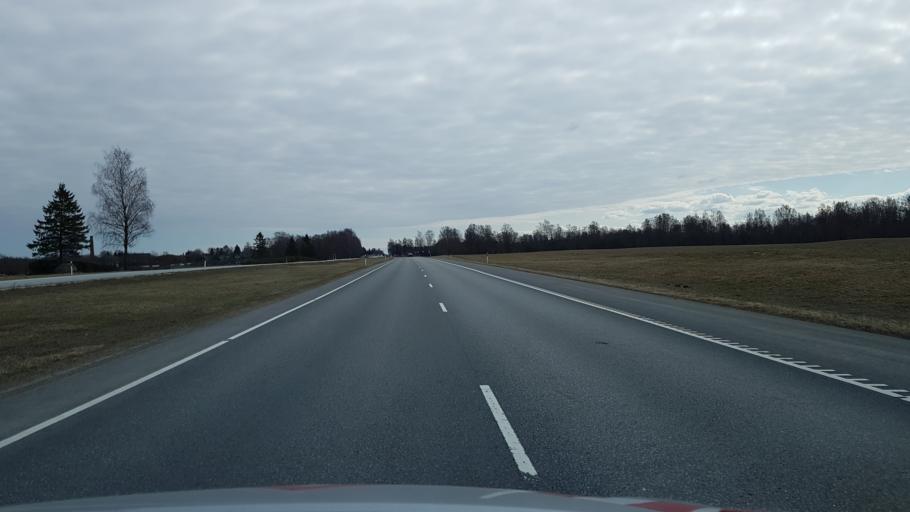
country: EE
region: Laeaene-Virumaa
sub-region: Kadrina vald
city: Kadrina
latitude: 59.4404
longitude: 26.1201
